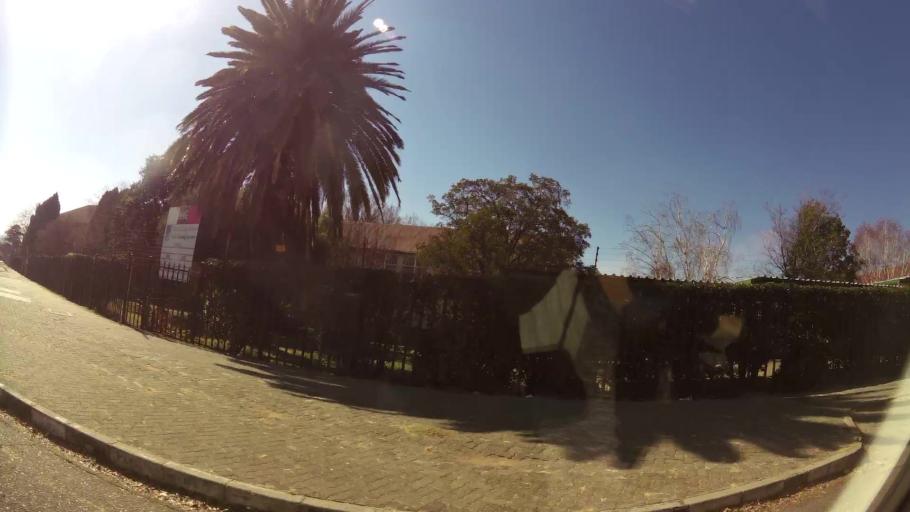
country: ZA
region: Gauteng
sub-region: City of Johannesburg Metropolitan Municipality
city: Johannesburg
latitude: -26.2497
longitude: 28.0676
